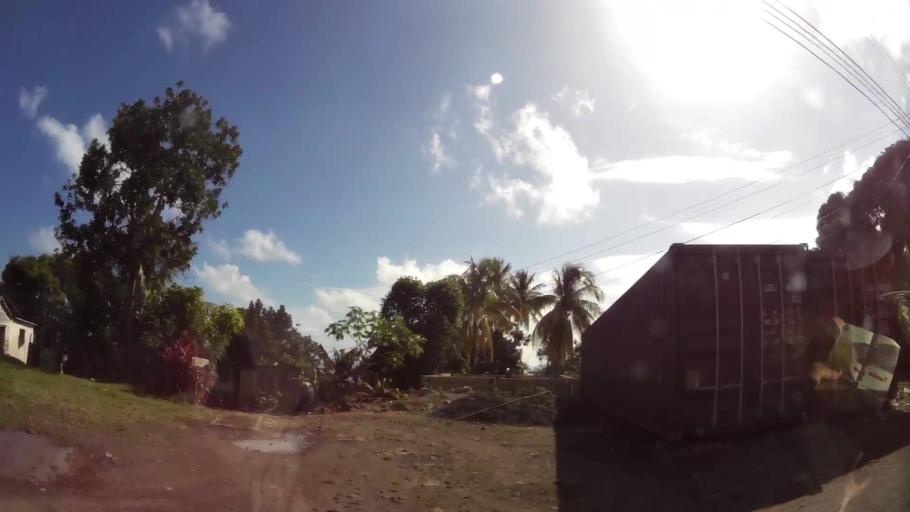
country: DM
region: Saint David
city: Castle Bruce
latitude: 15.4832
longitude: -61.2519
